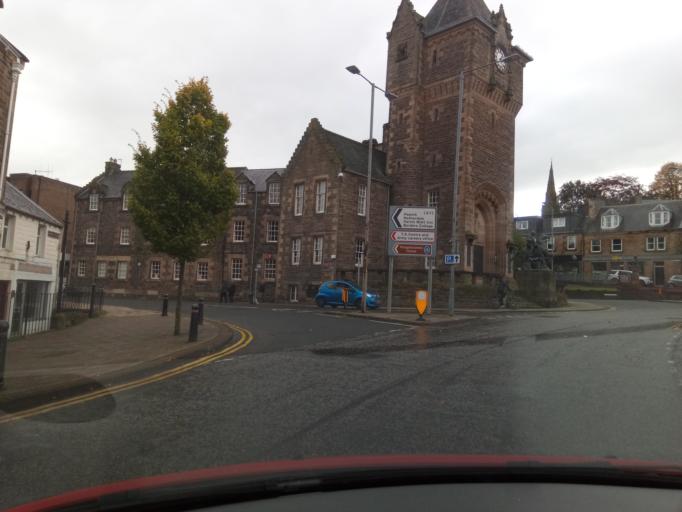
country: GB
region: Scotland
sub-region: The Scottish Borders
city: Galashiels
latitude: 55.6148
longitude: -2.8062
